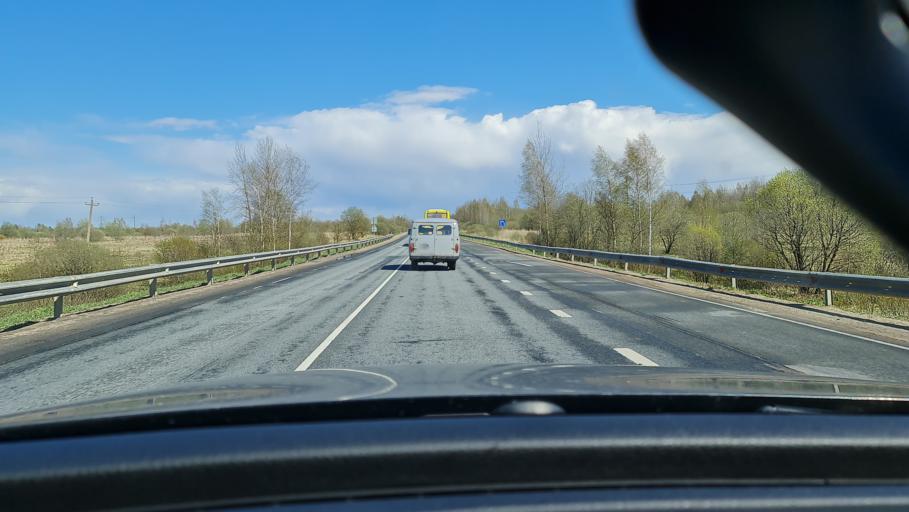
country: RU
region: Tverskaya
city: Rzhev
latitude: 56.2162
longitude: 34.2165
